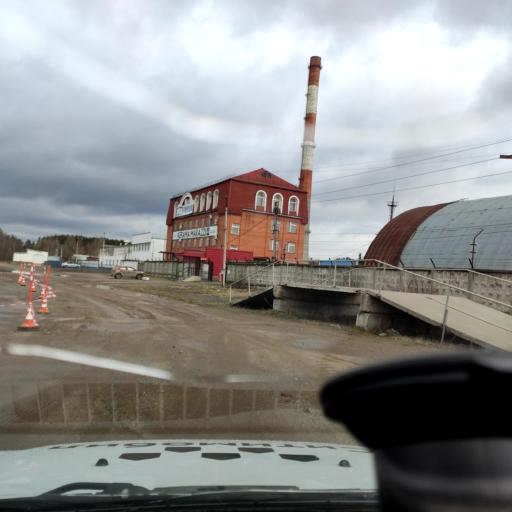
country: RU
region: Perm
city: Perm
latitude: 58.0385
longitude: 56.2061
